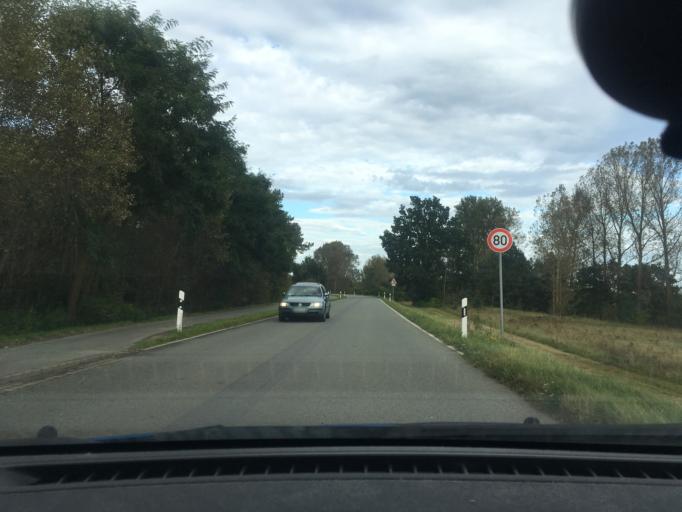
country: DE
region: Mecklenburg-Vorpommern
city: Boizenburg
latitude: 53.3532
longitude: 10.8141
